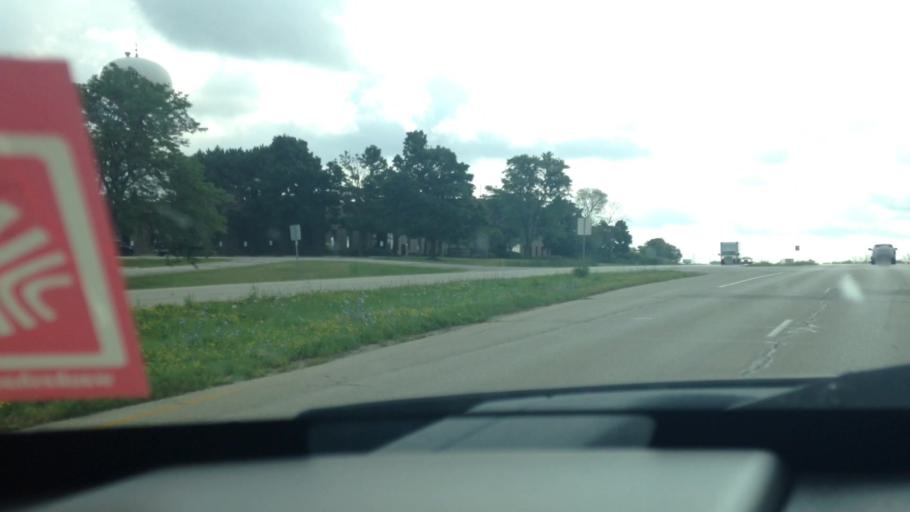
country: US
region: Wisconsin
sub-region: Waukesha County
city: Butler
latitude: 43.1178
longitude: -88.0747
